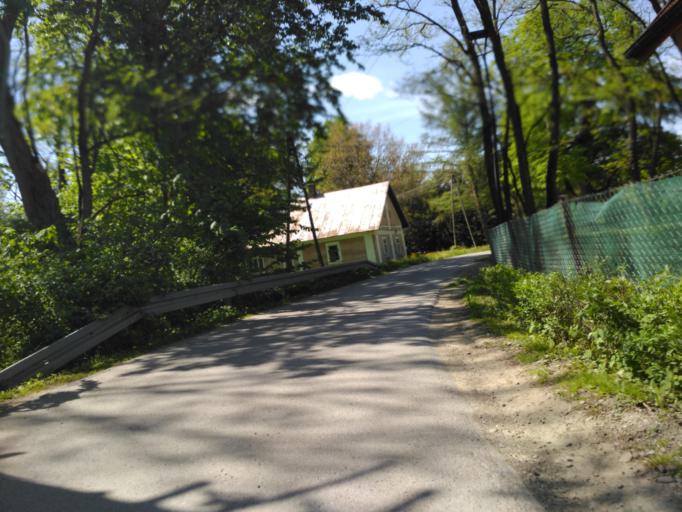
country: PL
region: Subcarpathian Voivodeship
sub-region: Powiat krosnienski
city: Miejsce Piastowe
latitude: 49.6142
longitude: 21.7592
